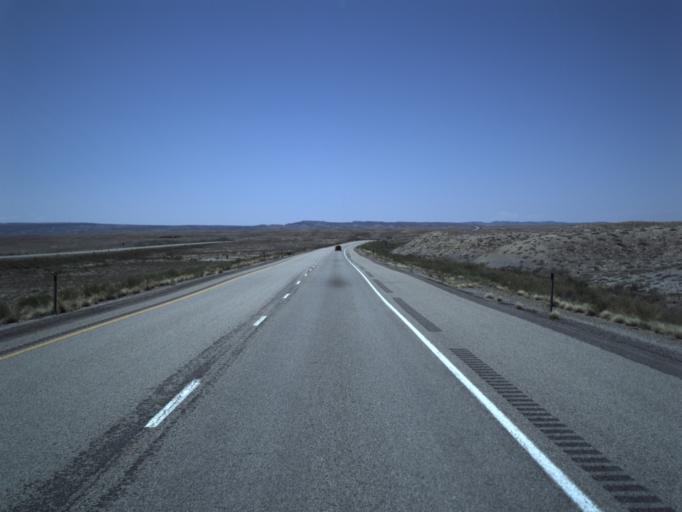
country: US
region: Utah
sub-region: Grand County
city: Moab
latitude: 38.9883
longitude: -109.3376
